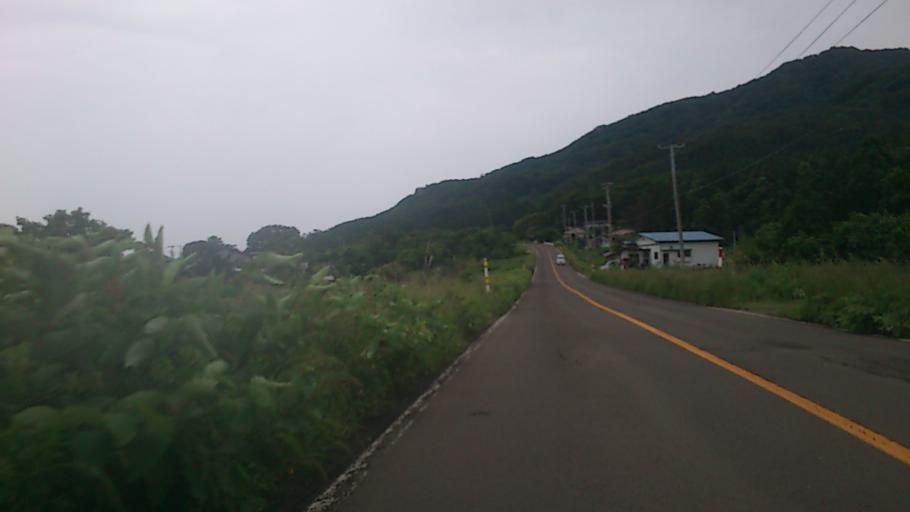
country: JP
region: Akita
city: Noshiromachi
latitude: 40.3798
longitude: 140.0025
